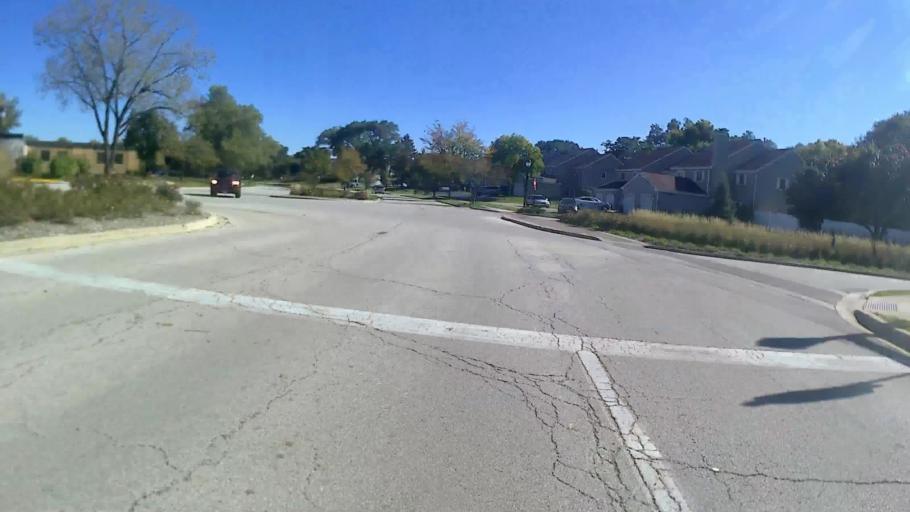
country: US
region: Illinois
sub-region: Cook County
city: Elk Grove Village
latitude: 42.0072
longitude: -87.9926
